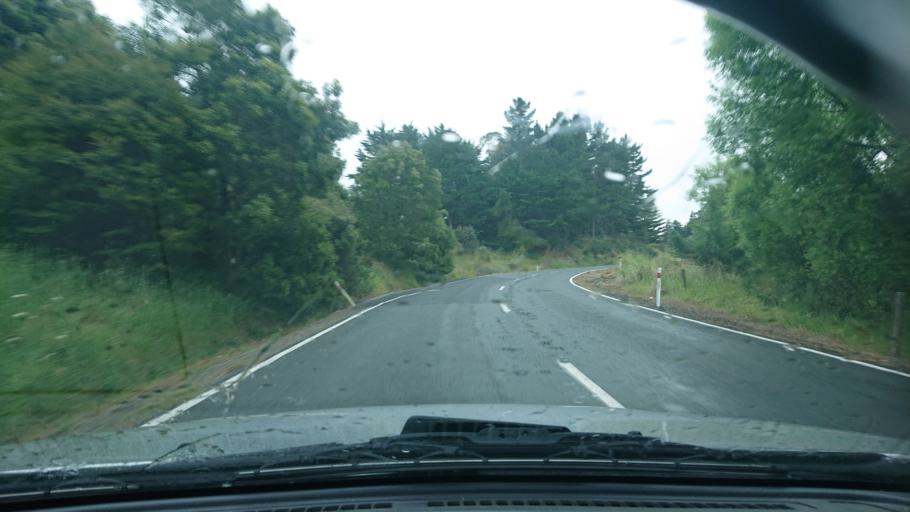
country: NZ
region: Auckland
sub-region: Auckland
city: Wellsford
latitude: -36.3326
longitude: 174.3818
